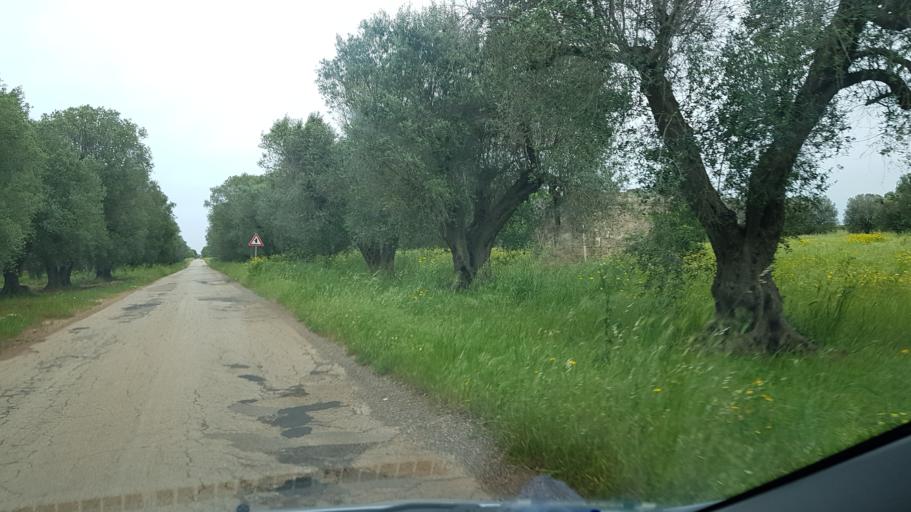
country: IT
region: Apulia
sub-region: Provincia di Brindisi
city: San Vito dei Normanni
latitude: 40.6220
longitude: 17.7603
